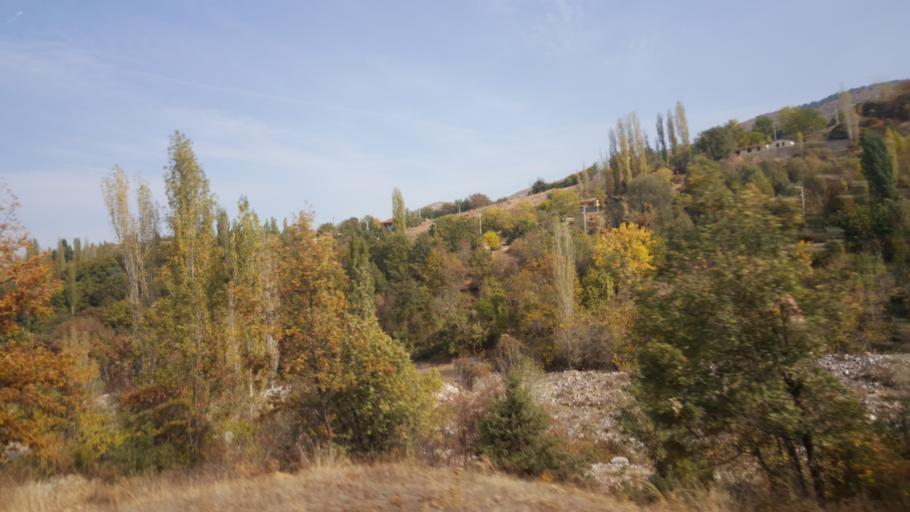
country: TR
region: Eskisehir
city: Mihaliccik
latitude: 39.9760
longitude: 31.3686
